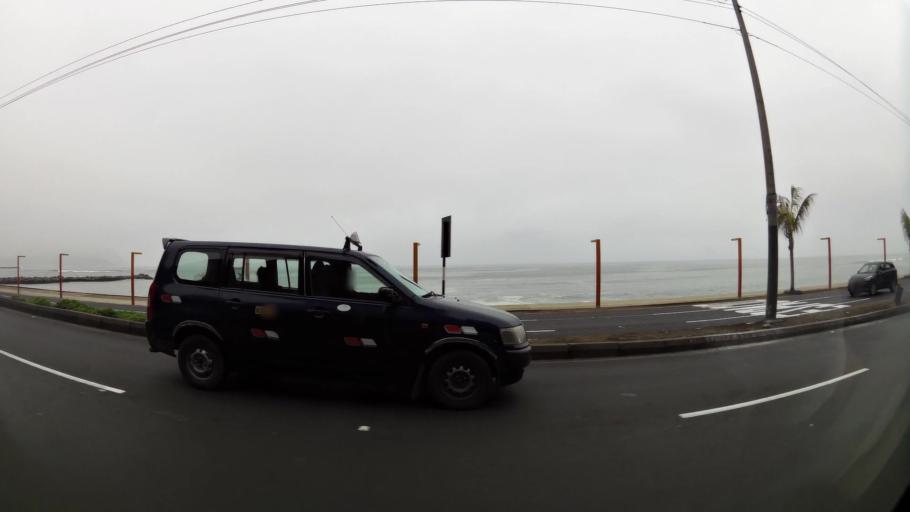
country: PE
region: Lima
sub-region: Lima
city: San Isidro
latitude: -12.1250
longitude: -77.0392
